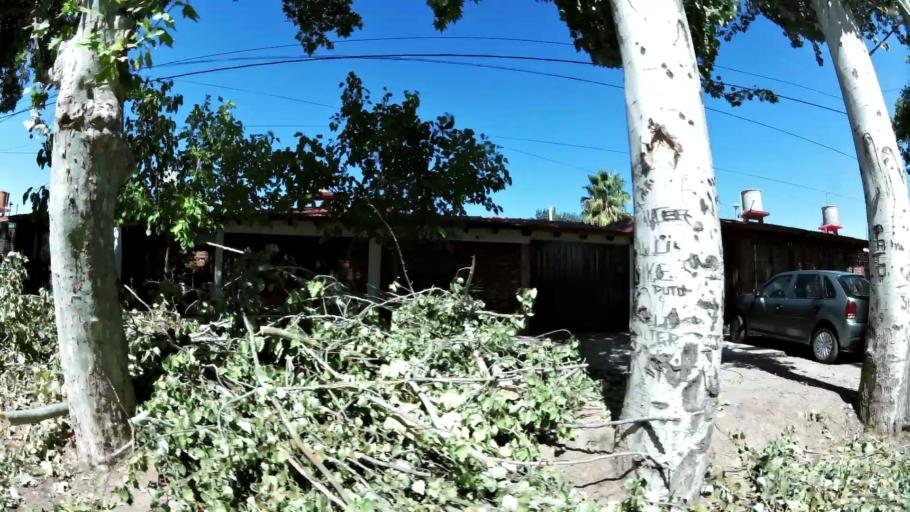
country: AR
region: Mendoza
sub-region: Departamento de Godoy Cruz
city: Godoy Cruz
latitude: -32.9746
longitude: -68.8389
